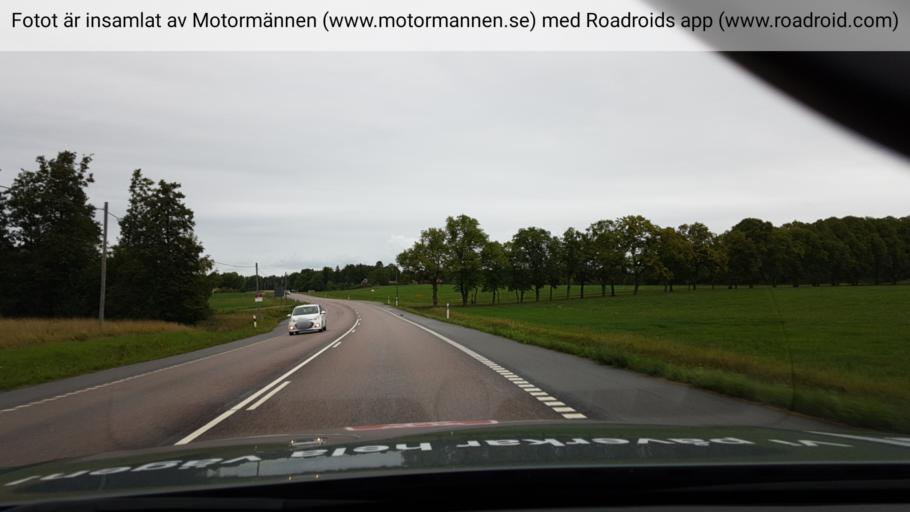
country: SE
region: Soedermanland
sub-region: Trosa Kommun
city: Vagnharad
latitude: 59.0073
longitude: 17.5964
